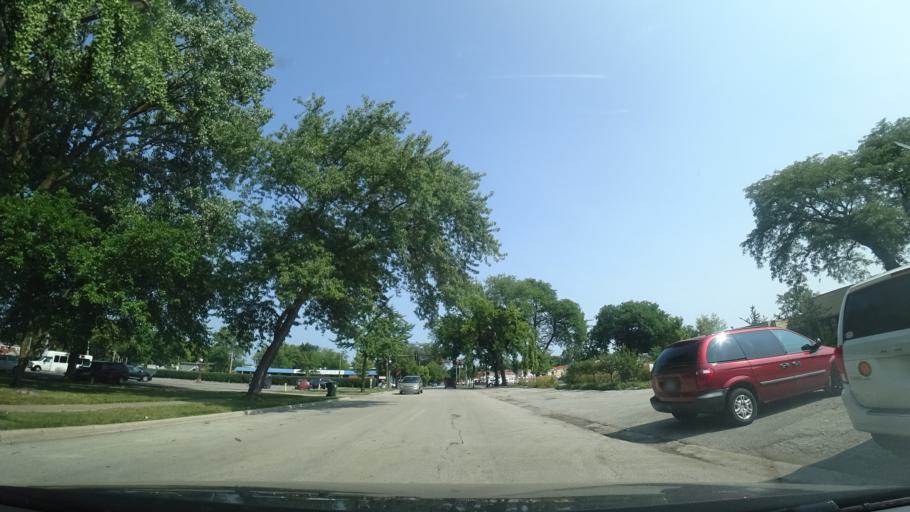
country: US
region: Illinois
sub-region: Cook County
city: Evanston
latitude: 42.0402
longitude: -87.7038
